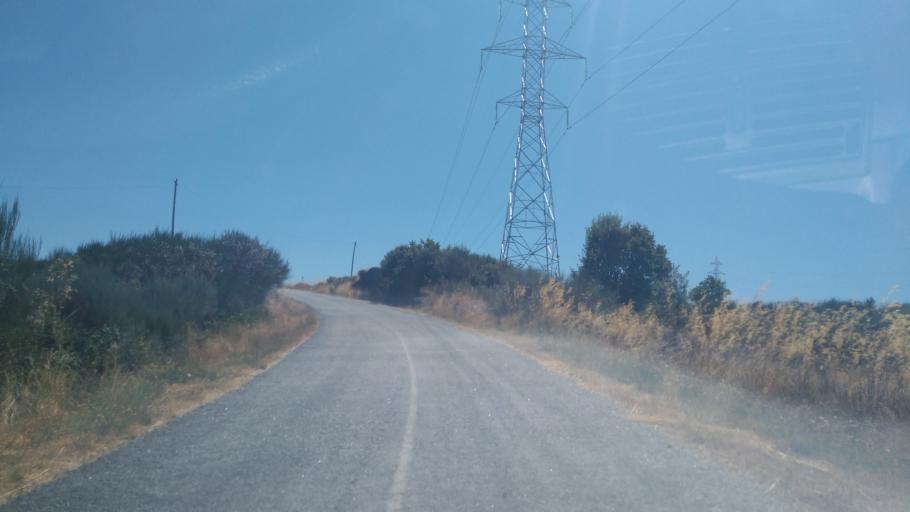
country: ES
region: Castille and Leon
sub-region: Provincia de Salamanca
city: Mieza
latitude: 41.2045
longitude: -6.6735
